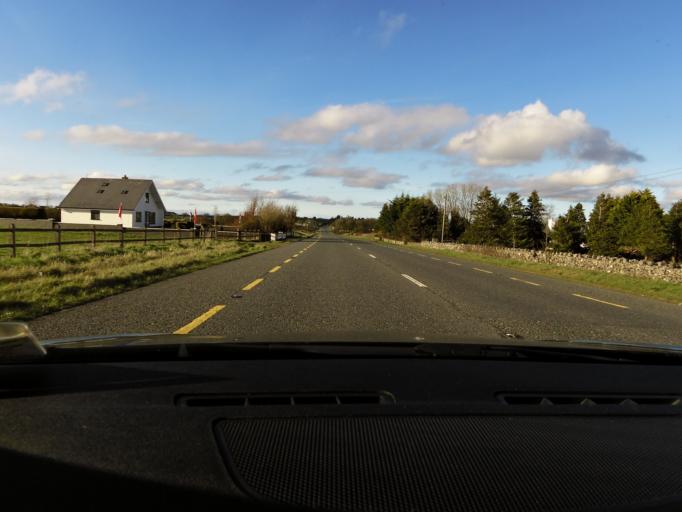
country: IE
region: Connaught
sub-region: Roscommon
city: Roscommon
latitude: 53.6714
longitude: -8.1976
